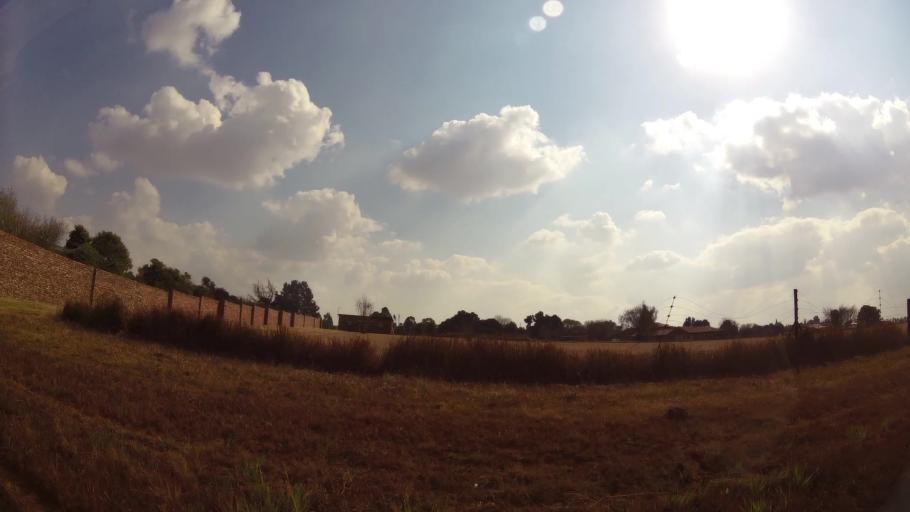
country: ZA
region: Mpumalanga
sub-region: Nkangala District Municipality
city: Delmas
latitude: -26.1538
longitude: 28.5590
